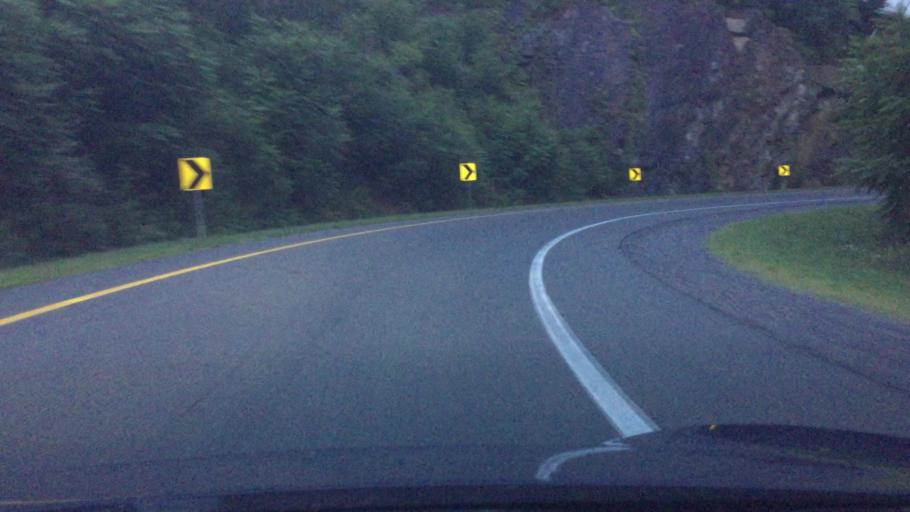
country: US
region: Virginia
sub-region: Wythe County
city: Wytheville
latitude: 36.9487
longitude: -81.0506
